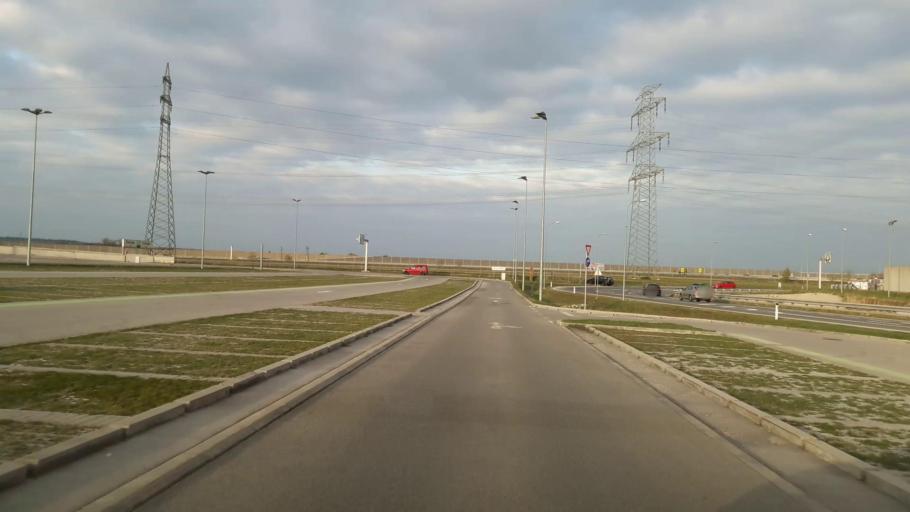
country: AT
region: Lower Austria
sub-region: Politischer Bezirk Mistelbach
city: Grossebersdorf
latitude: 48.3445
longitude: 16.4647
